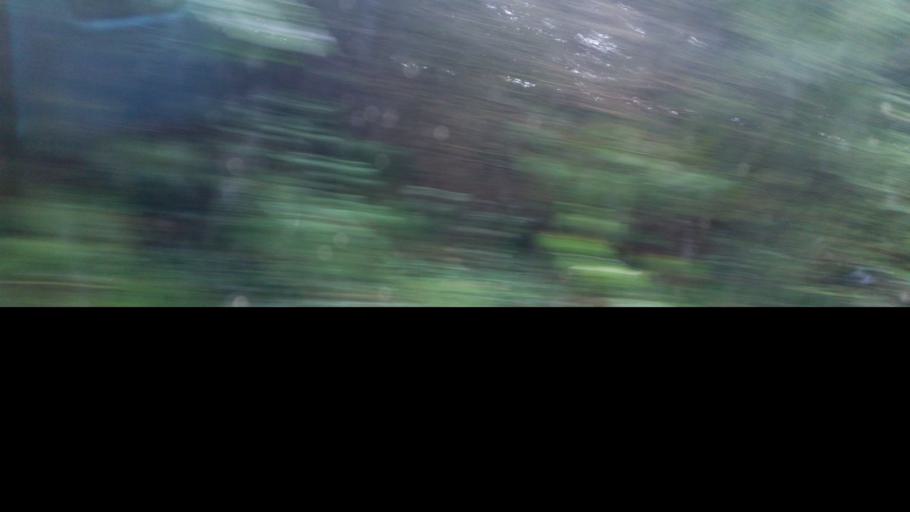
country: IE
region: Leinster
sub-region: Kilkenny
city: Graiguenamanagh
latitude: 52.5459
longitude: -6.9473
